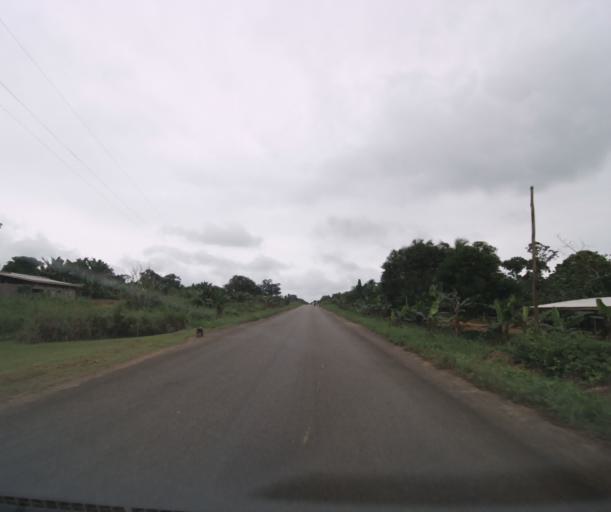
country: CM
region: Littoral
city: Edea
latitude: 3.7300
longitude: 10.1127
